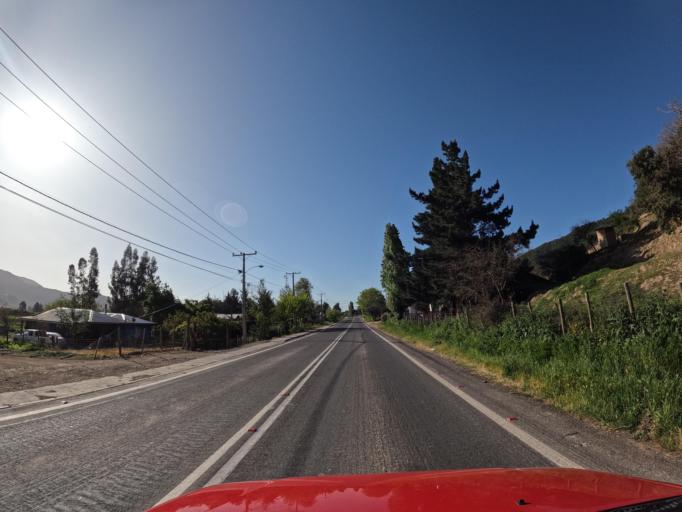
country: CL
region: Maule
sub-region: Provincia de Curico
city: Teno
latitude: -34.7996
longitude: -71.2243
